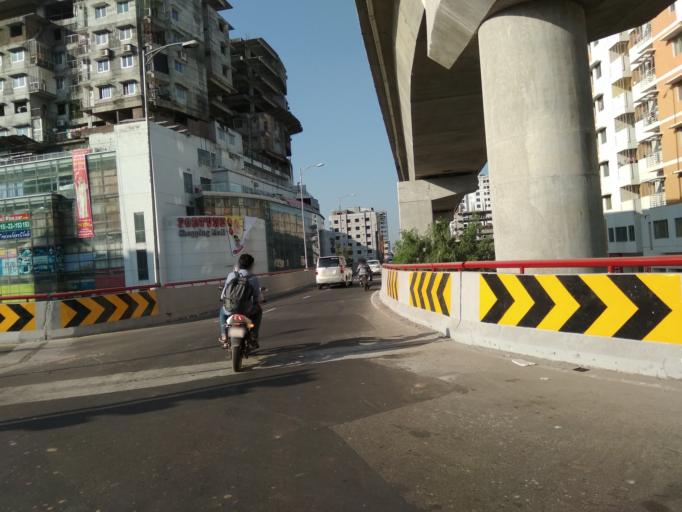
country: BD
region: Dhaka
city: Paltan
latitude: 23.7455
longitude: 90.4124
